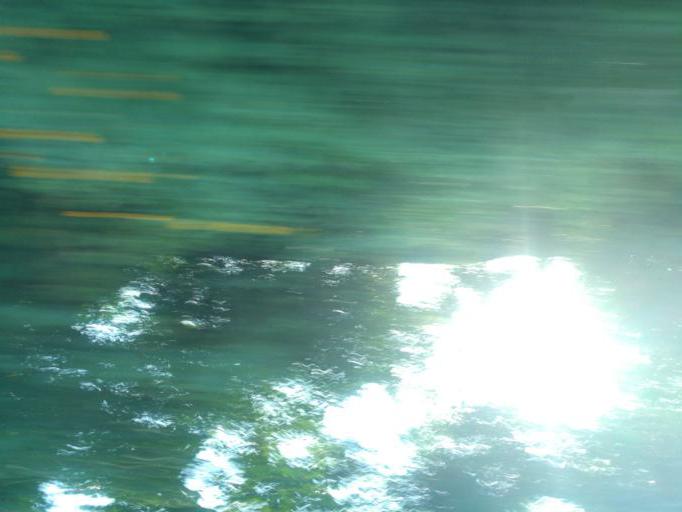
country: NG
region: Ogun
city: Abeokuta
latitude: 7.2420
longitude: 3.3007
